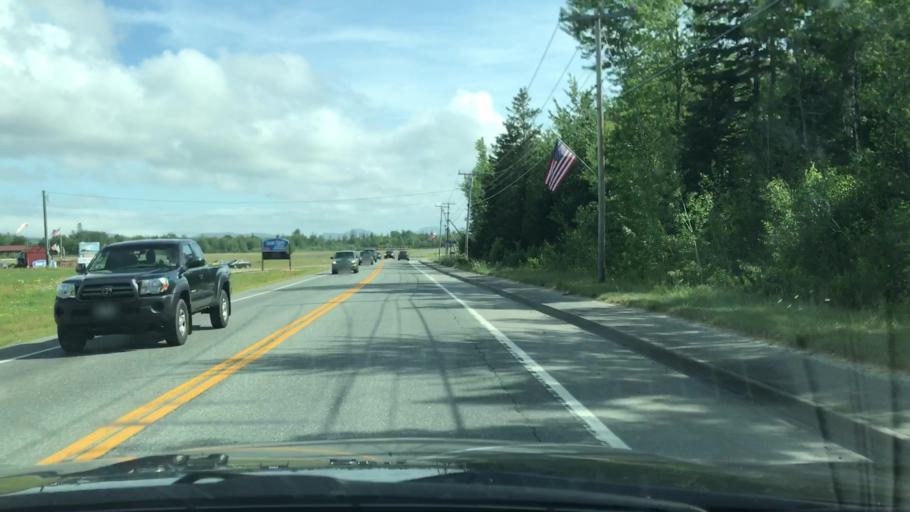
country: US
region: Maine
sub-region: Hancock County
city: Trenton
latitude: 44.4471
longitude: -68.3696
